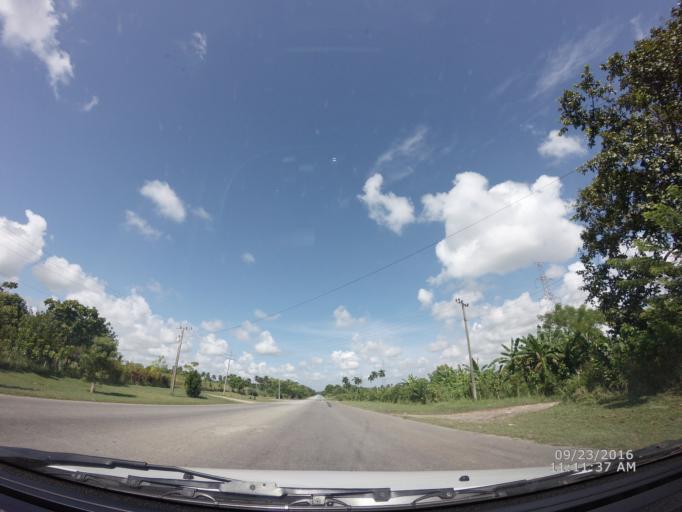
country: CU
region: La Habana
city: Arroyo Naranjo
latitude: 23.0261
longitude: -82.2719
